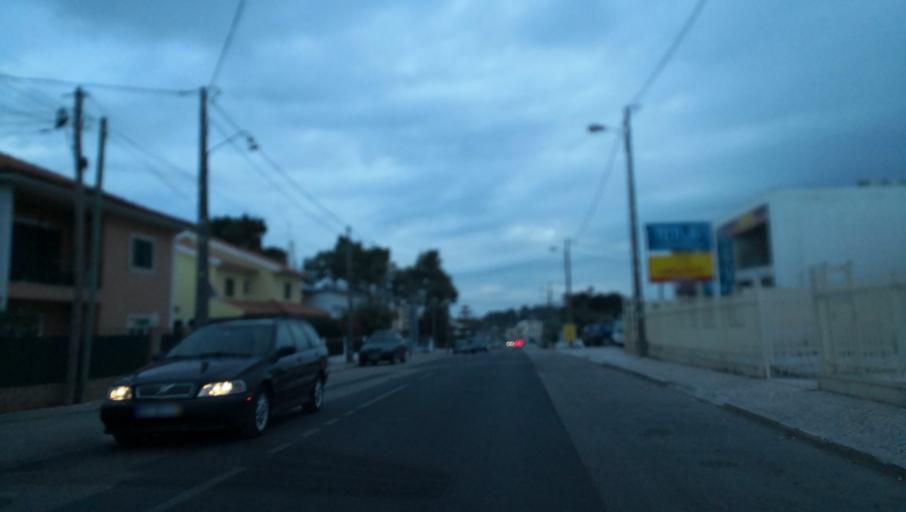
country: PT
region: Setubal
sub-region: Almada
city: Charneca
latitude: 38.6035
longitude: -9.1863
